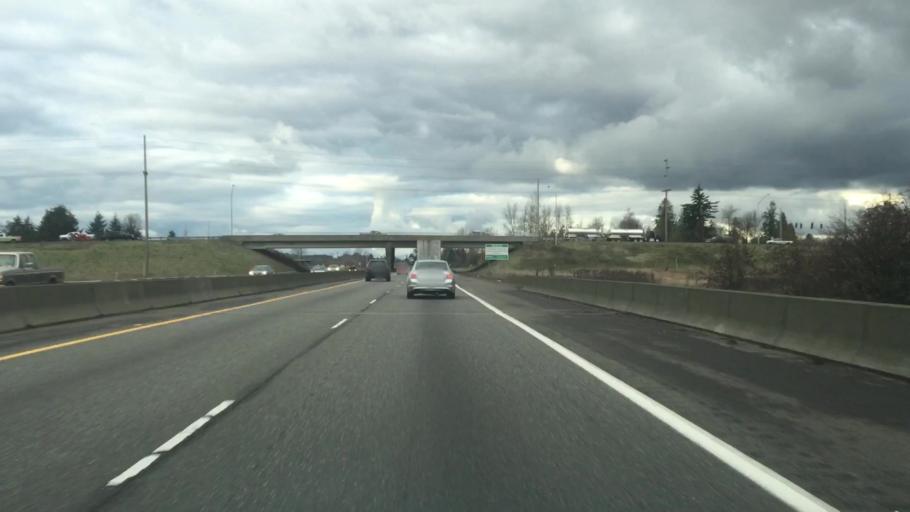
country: US
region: Washington
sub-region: Lewis County
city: Chehalis
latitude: 46.6588
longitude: -122.9779
